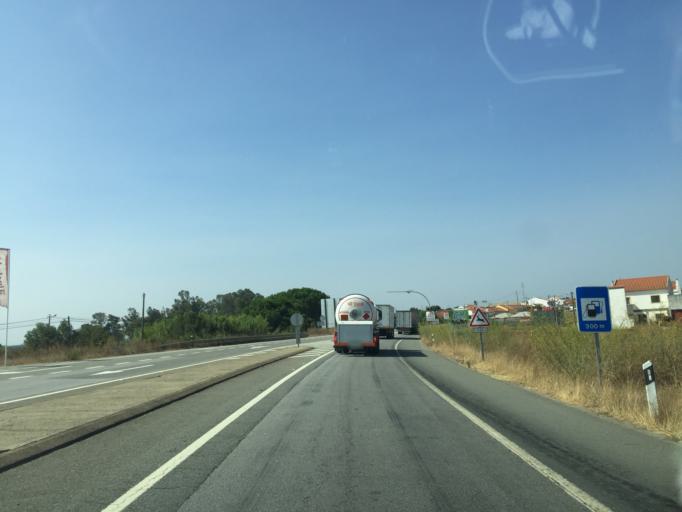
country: PT
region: Beja
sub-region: Aljustrel
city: Aljustrel
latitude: 37.9434
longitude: -8.3796
